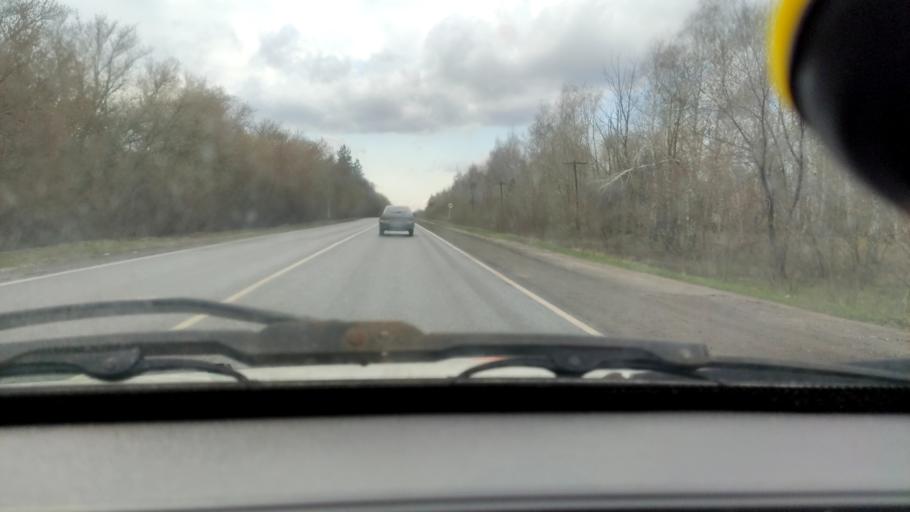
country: RU
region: Samara
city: Povolzhskiy
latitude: 53.6077
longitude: 49.6107
